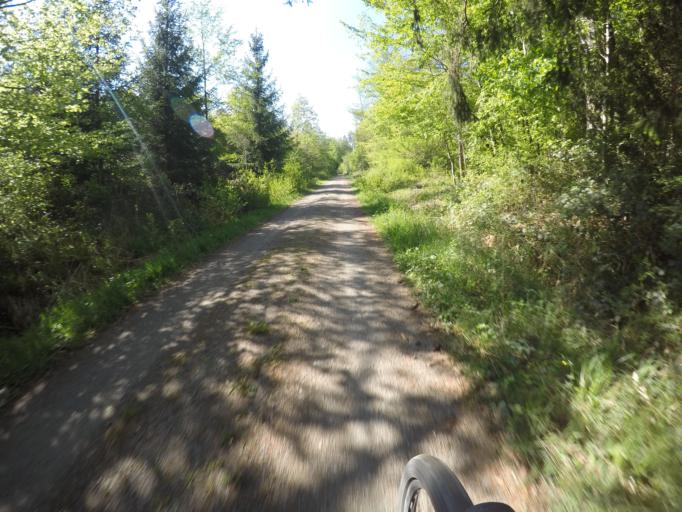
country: DE
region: Baden-Wuerttemberg
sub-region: Tuebingen Region
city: Dettenhausen
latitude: 48.5776
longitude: 9.0932
